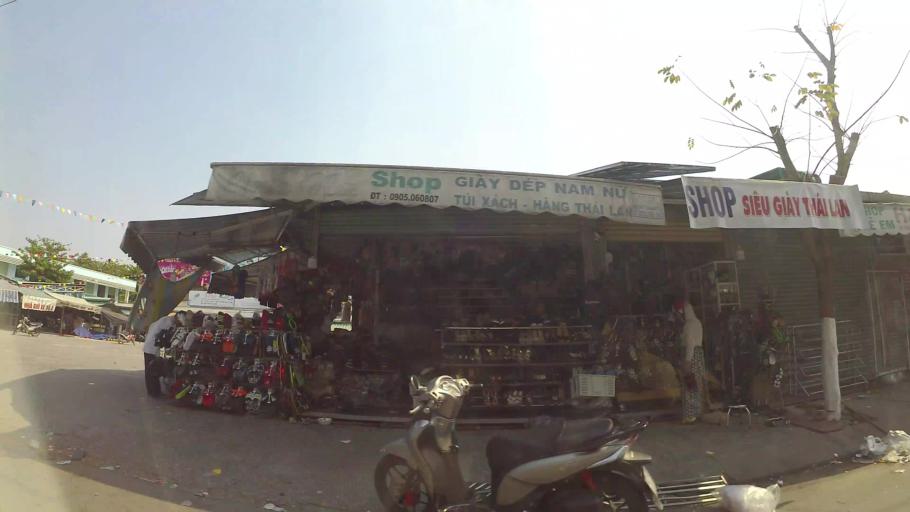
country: VN
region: Da Nang
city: Cam Le
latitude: 16.0139
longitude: 108.2067
